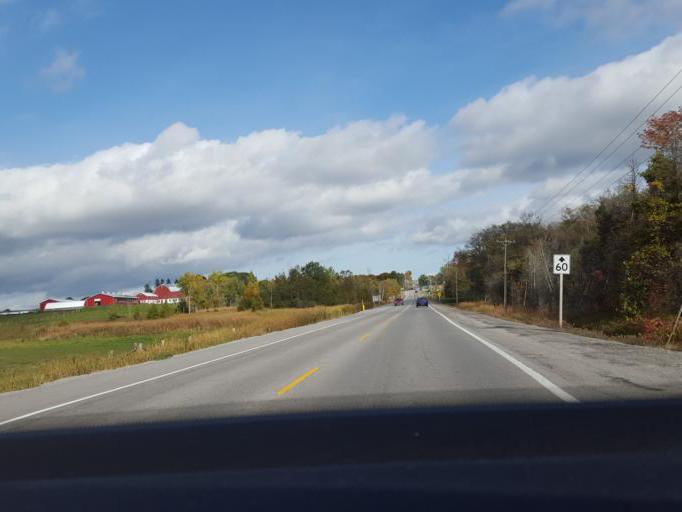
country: CA
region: Ontario
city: Oshawa
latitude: 43.9913
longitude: -78.6195
